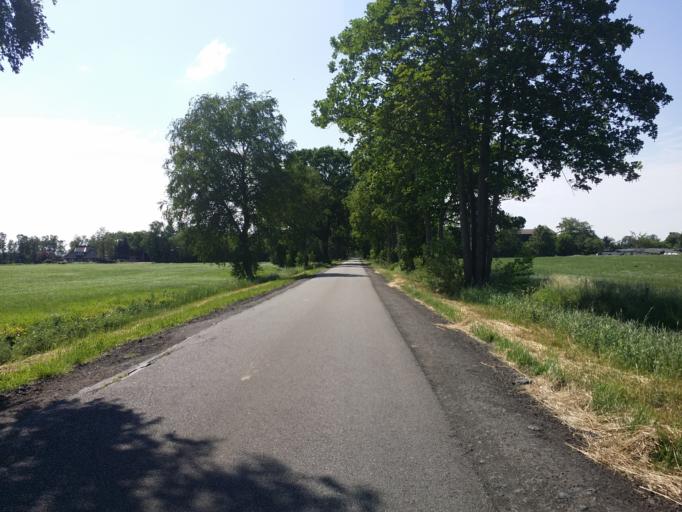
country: DE
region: Lower Saxony
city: Oldenburg
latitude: 53.2060
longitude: 8.3172
